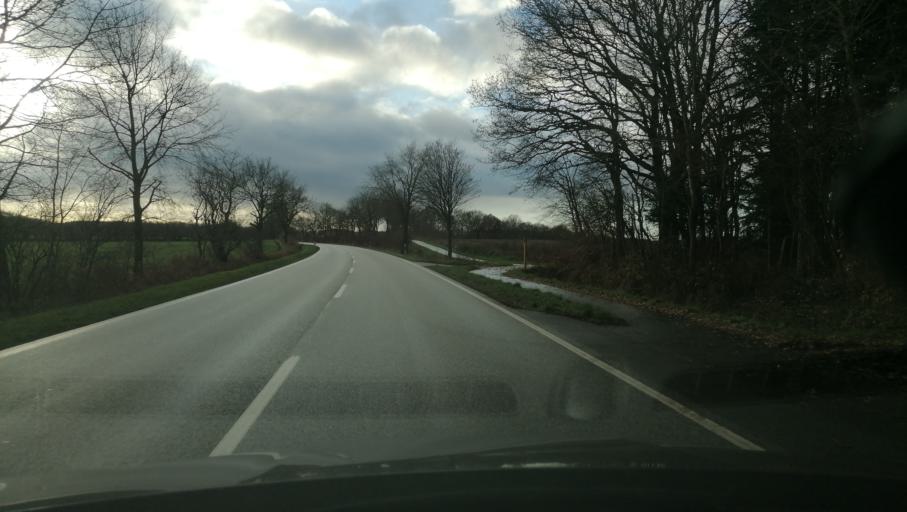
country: DE
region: Schleswig-Holstein
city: Sarzbuttel
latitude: 54.1098
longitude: 9.2012
